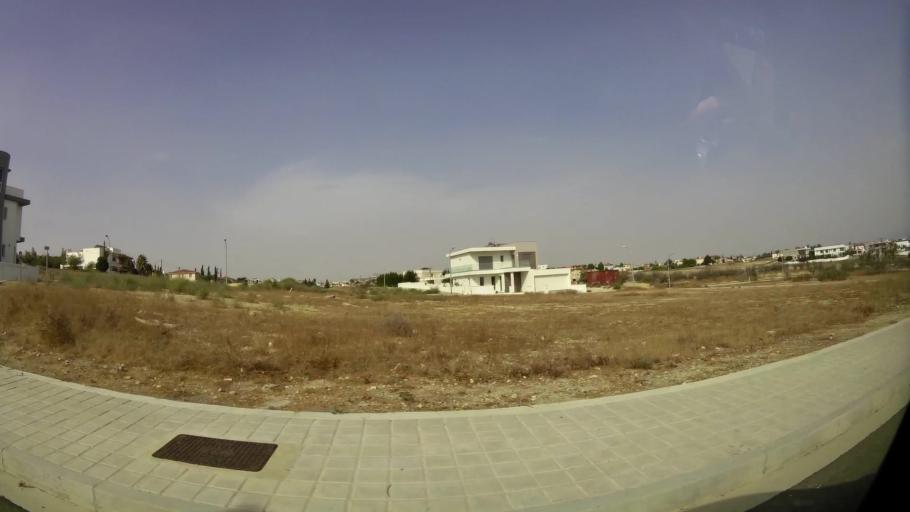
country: CY
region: Lefkosia
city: Geri
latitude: 35.0727
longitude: 33.3980
